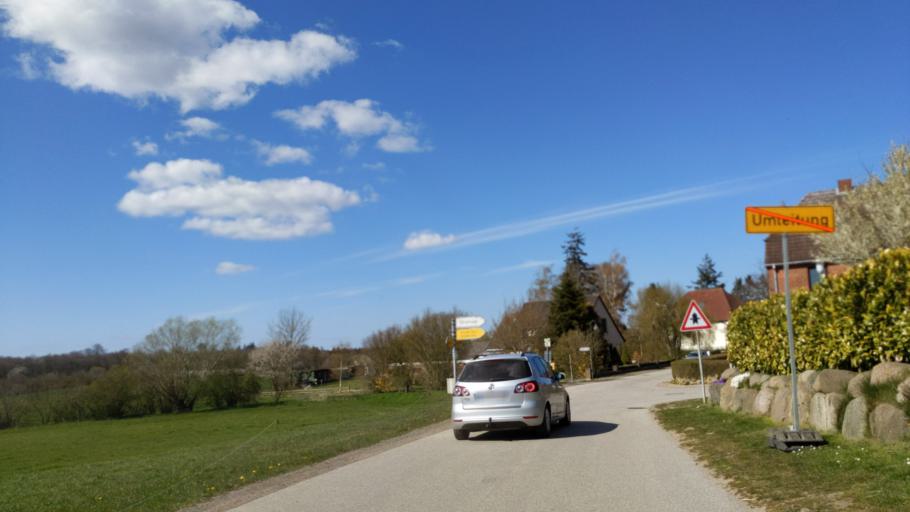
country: DE
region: Schleswig-Holstein
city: Kasseedorf
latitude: 54.1369
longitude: 10.6865
